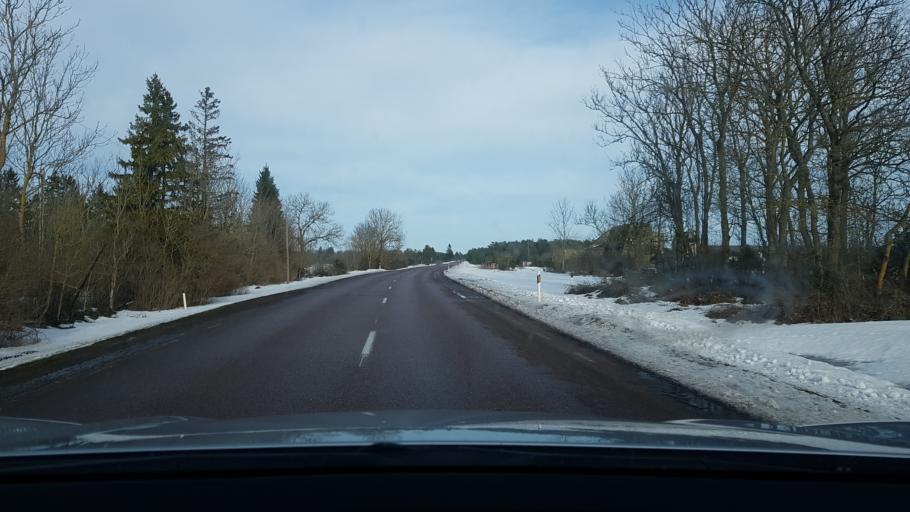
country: EE
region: Saare
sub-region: Kuressaare linn
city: Kuressaare
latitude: 58.3290
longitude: 22.5587
